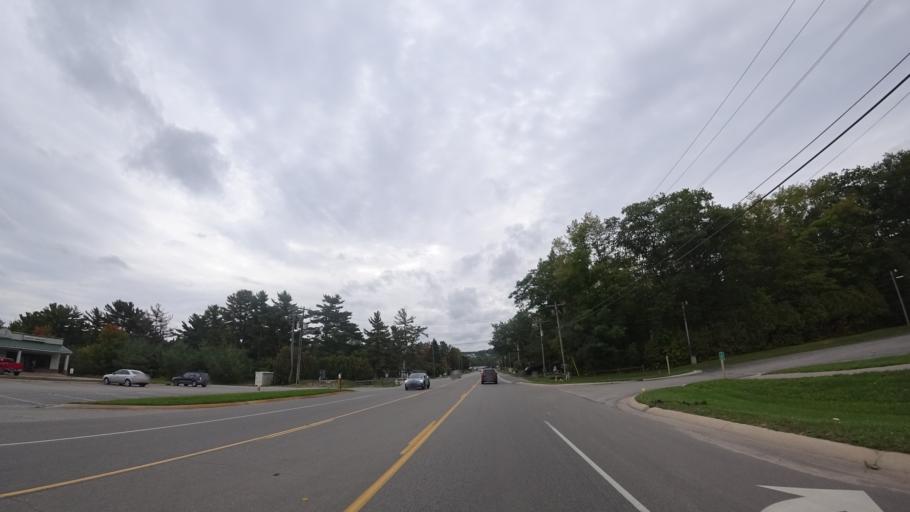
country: US
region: Michigan
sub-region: Emmet County
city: Petoskey
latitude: 45.4031
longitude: -84.9021
